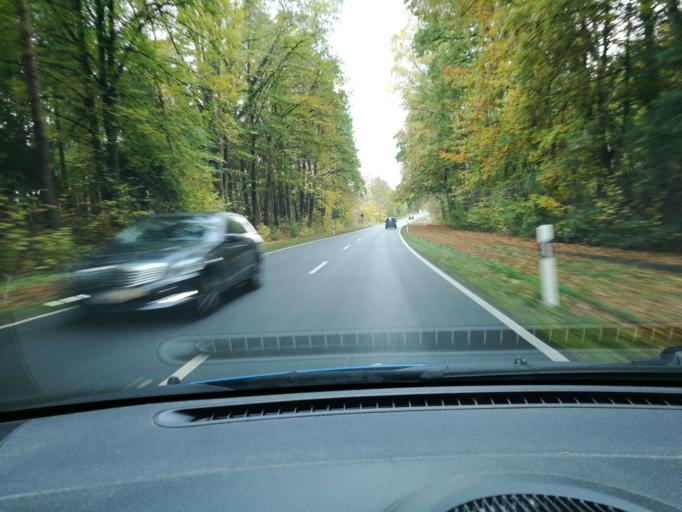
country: DE
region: Schleswig-Holstein
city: Gross Sarau
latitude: 53.7787
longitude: 10.7483
